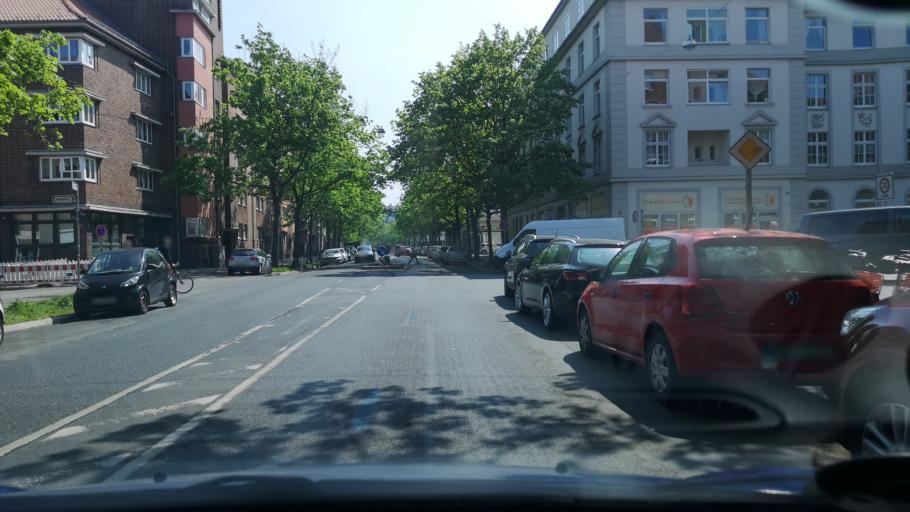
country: DE
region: Lower Saxony
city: Hannover
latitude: 52.3934
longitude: 9.7292
